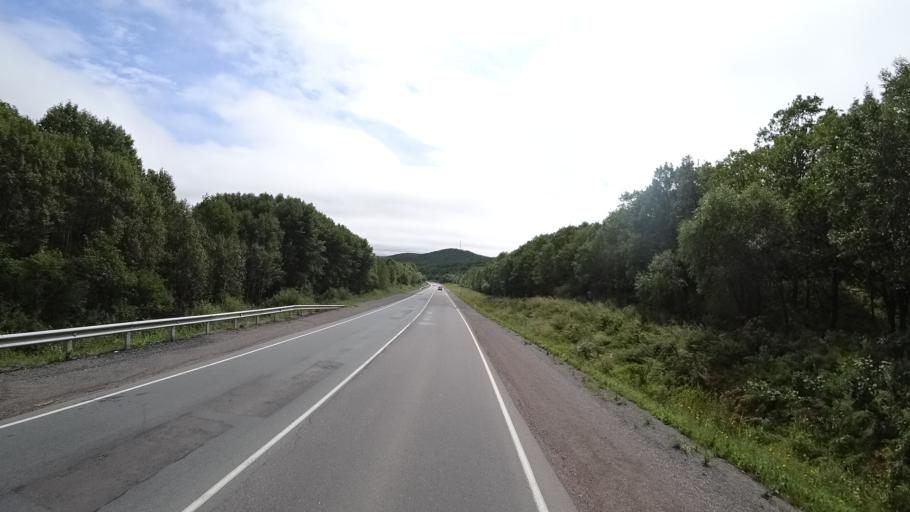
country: RU
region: Primorskiy
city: Lyalichi
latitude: 44.1201
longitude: 132.4198
